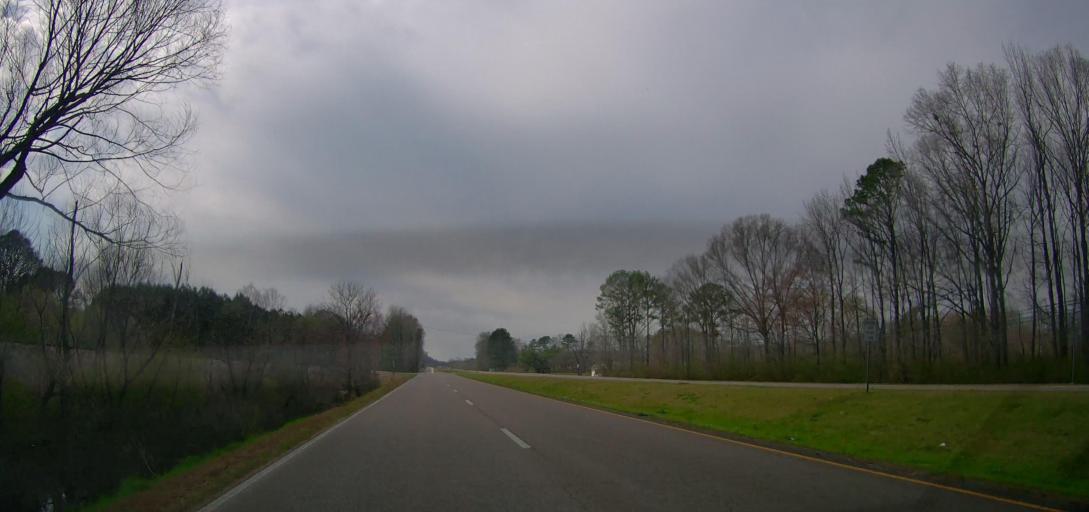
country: US
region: Alabama
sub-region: Walker County
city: Carbon Hill
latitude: 33.8797
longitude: -87.5042
